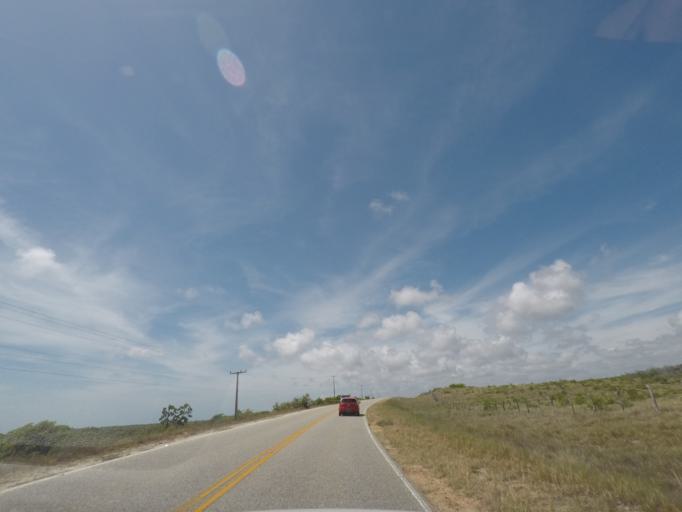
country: BR
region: Sergipe
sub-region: Sao Cristovao
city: Sao Cristovao
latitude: -11.1535
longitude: -37.2001
